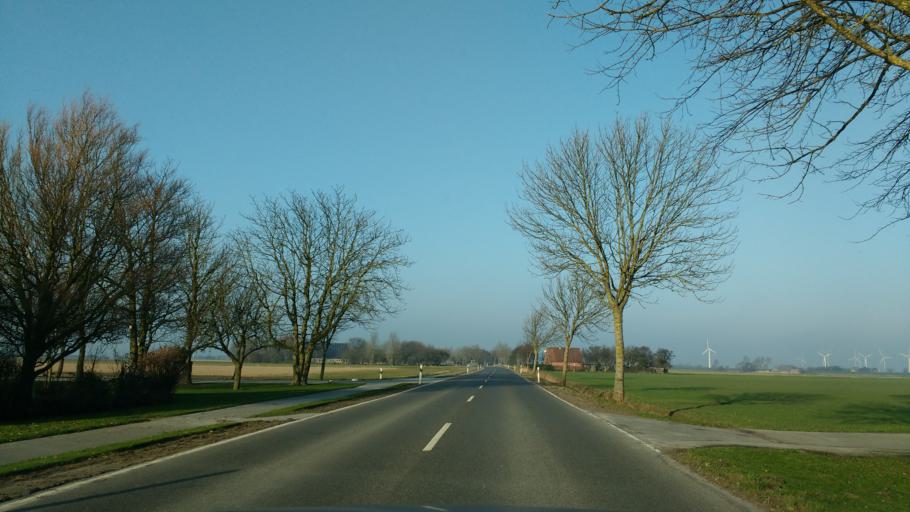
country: DE
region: Schleswig-Holstein
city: Friedrichskoog
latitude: 53.9836
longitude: 8.9149
